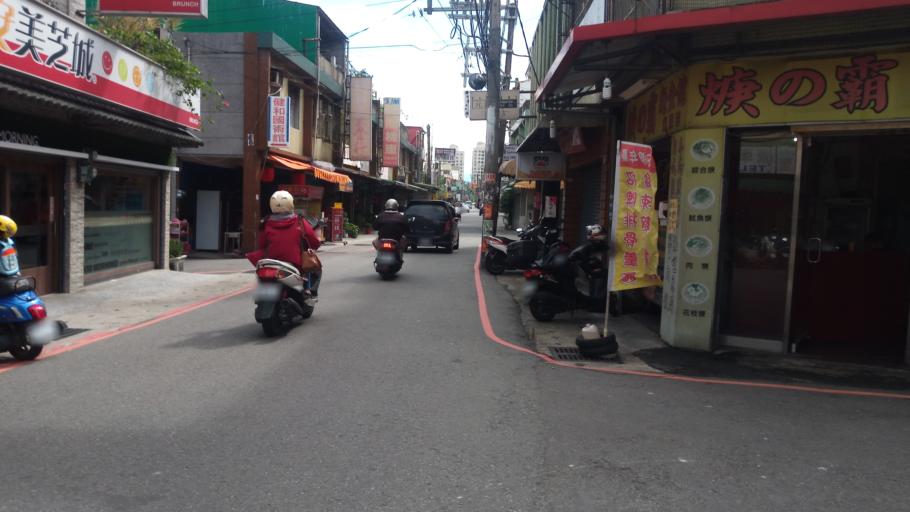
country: TW
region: Taiwan
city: Daxi
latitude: 24.9371
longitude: 121.2495
